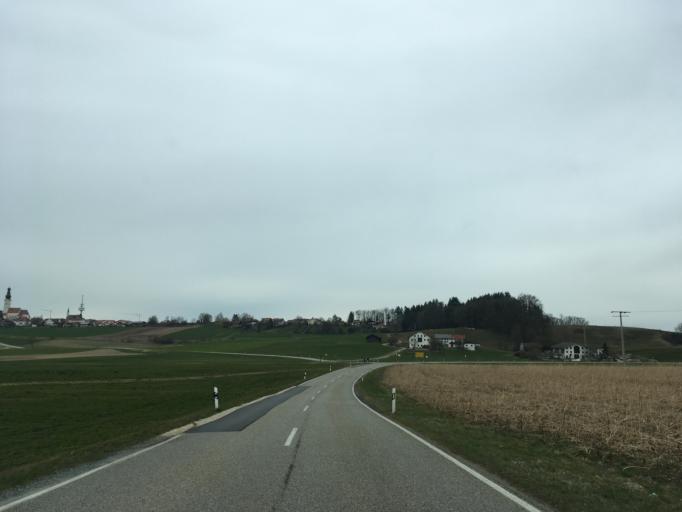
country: DE
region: Bavaria
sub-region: Upper Bavaria
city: Schnaitsee
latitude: 48.0623
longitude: 12.3798
